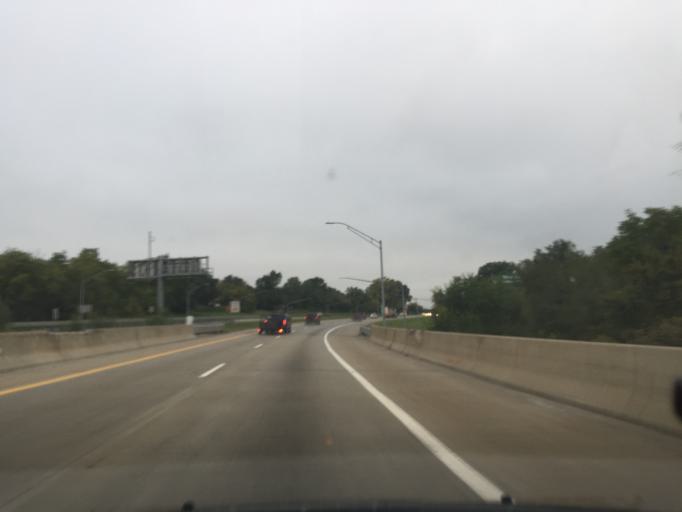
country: US
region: Michigan
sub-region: Oakland County
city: Pontiac
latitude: 42.6425
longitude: -83.2597
